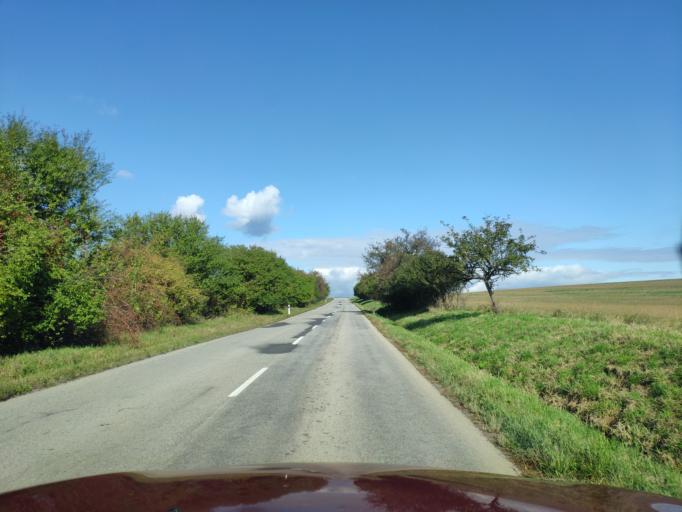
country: SK
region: Presovsky
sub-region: Okres Presov
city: Presov
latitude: 48.8929
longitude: 21.2596
